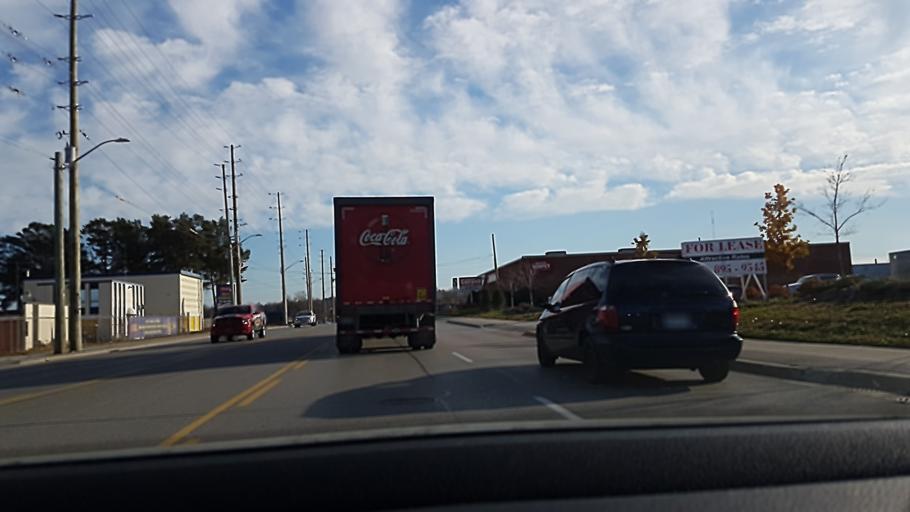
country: CA
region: Ontario
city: Barrie
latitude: 44.3771
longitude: -79.7006
